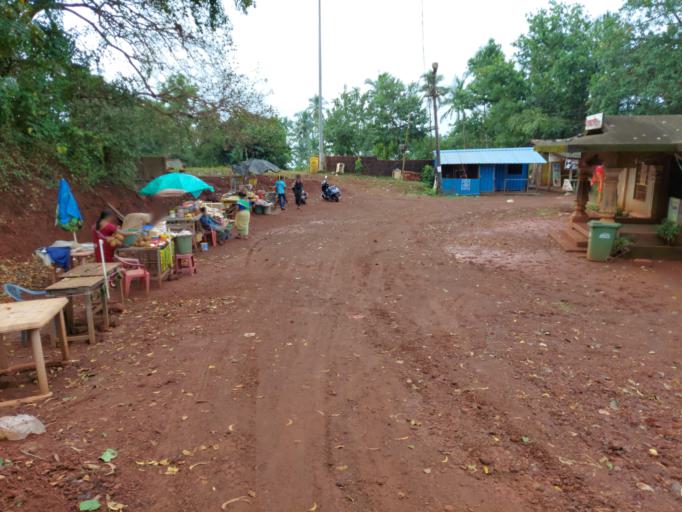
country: IN
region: Goa
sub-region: North Goa
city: Arambol
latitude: 15.7431
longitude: 73.6576
